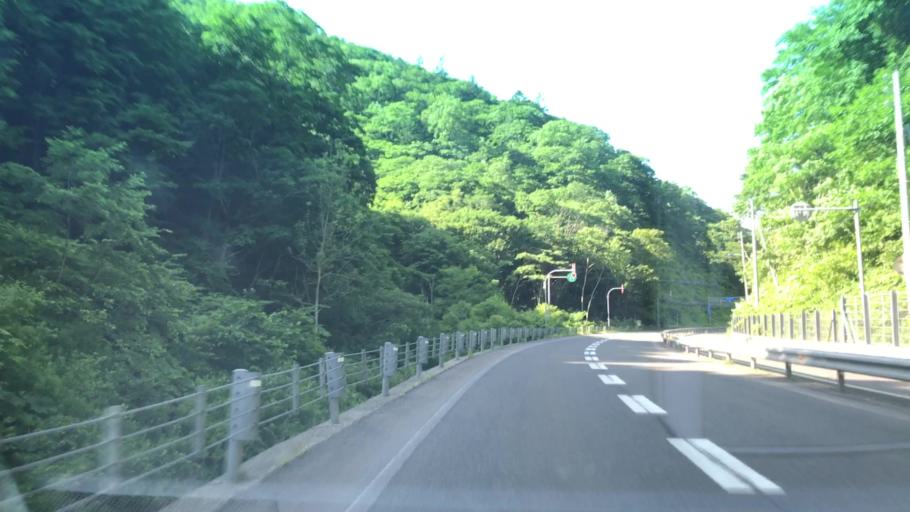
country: JP
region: Hokkaido
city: Iwanai
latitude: 43.0402
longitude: 140.6797
